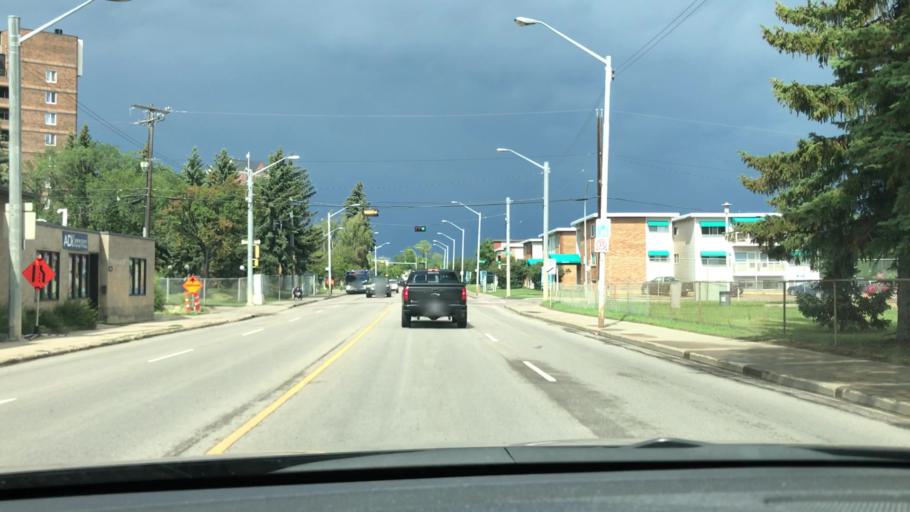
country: CA
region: Alberta
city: Edmonton
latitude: 53.5466
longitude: -113.4773
